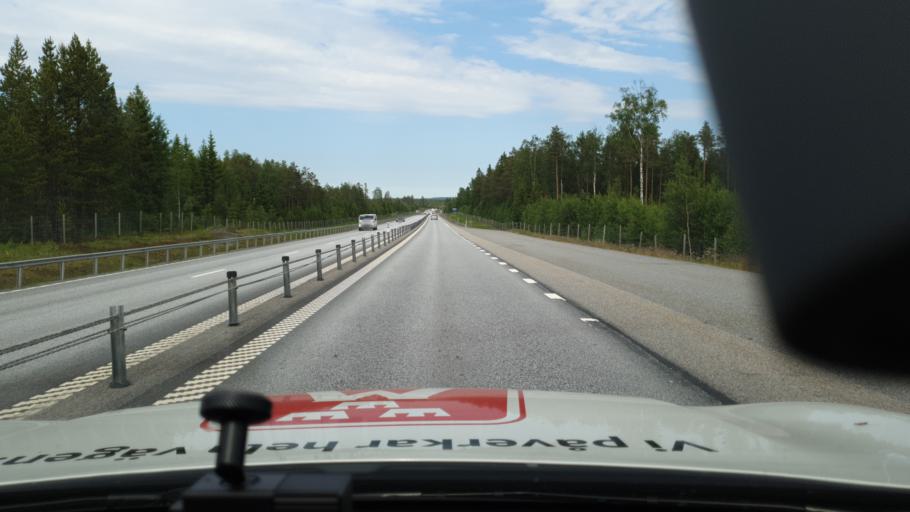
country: SE
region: Vaesterbotten
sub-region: Umea Kommun
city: Hoernefors
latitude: 63.6561
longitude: 19.9549
